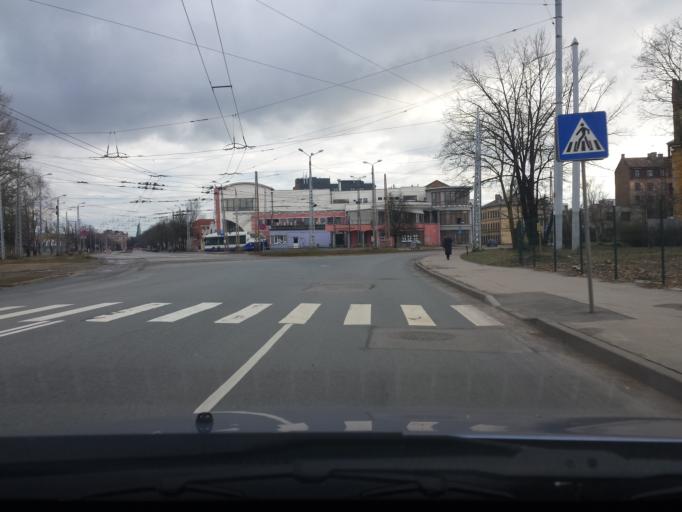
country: LV
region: Riga
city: Riga
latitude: 56.9686
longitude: 24.1067
